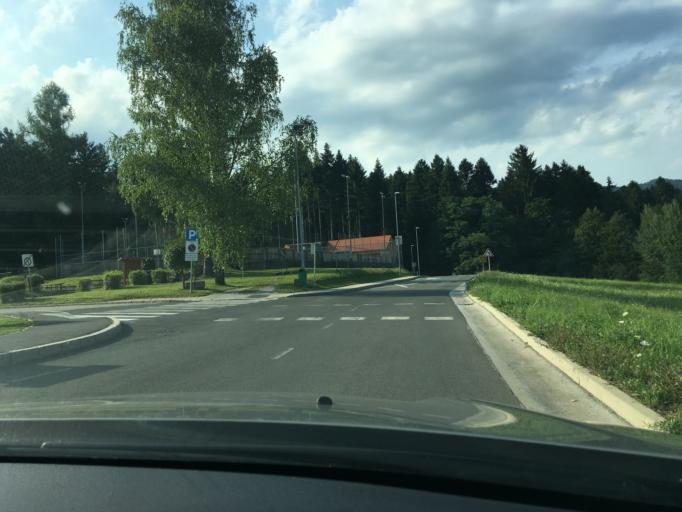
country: SI
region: Dolenjske Toplice
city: Dolenjske Toplice
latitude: 45.7574
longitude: 15.0543
